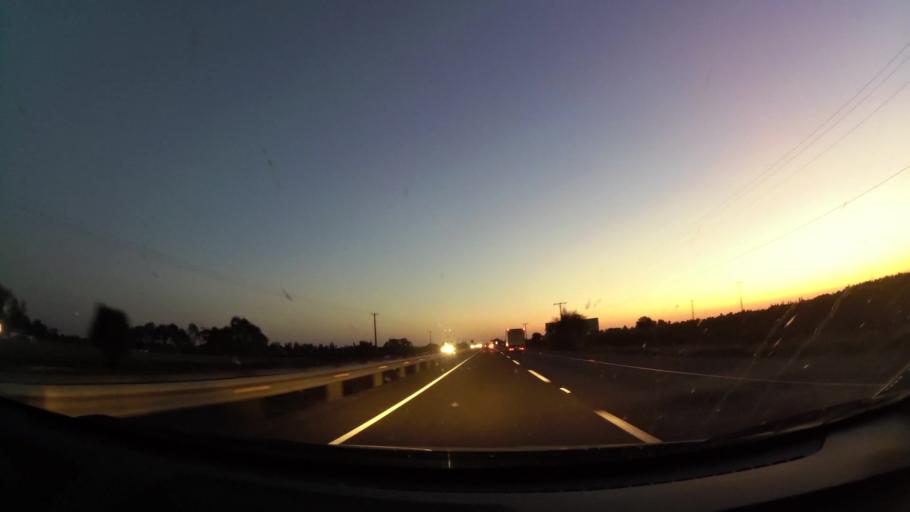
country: CL
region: Maule
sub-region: Provincia de Linares
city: Parral
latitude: -36.3104
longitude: -71.8321
